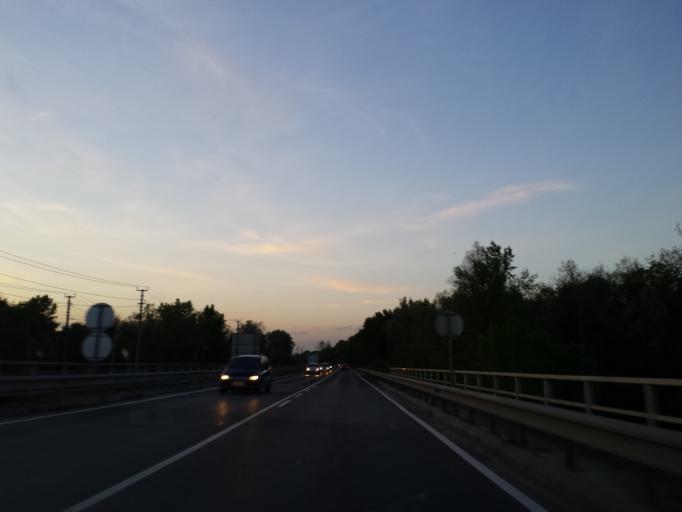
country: AT
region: Lower Austria
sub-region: Politischer Bezirk Tulln
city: Tulln
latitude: 48.3423
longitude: 16.0601
